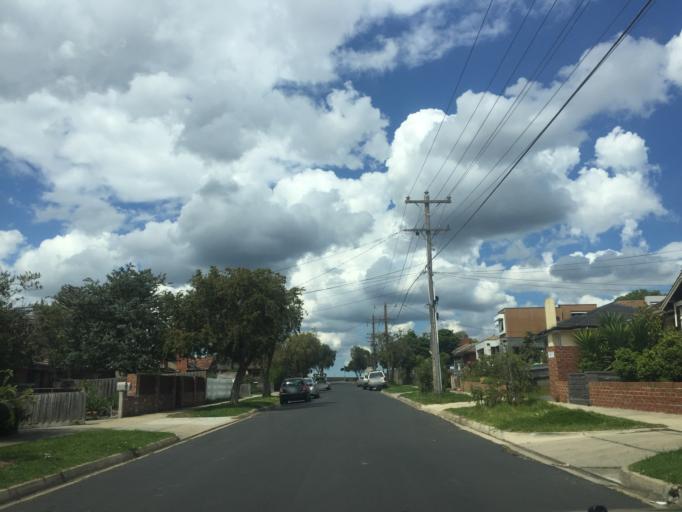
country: AU
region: Victoria
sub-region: Darebin
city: Kingsbury
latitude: -37.7231
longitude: 145.0265
